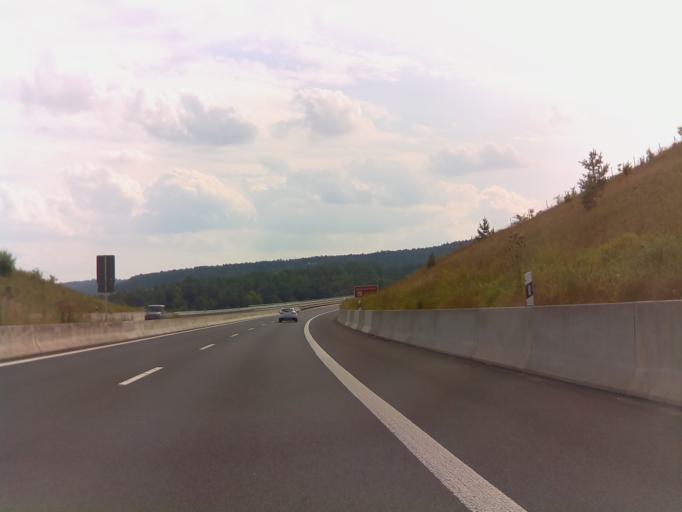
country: DE
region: Bavaria
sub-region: Regierungsbezirk Unterfranken
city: Hollstadt
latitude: 50.3480
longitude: 10.3146
